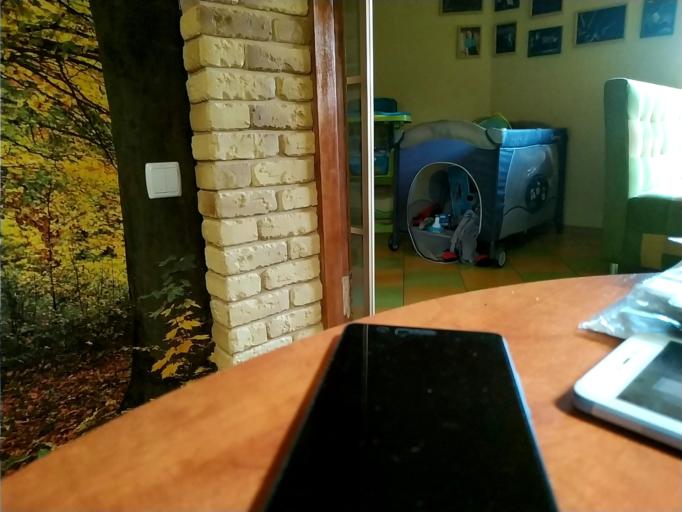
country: RU
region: Kaluga
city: Seredeyskiy
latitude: 53.8198
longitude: 35.3859
